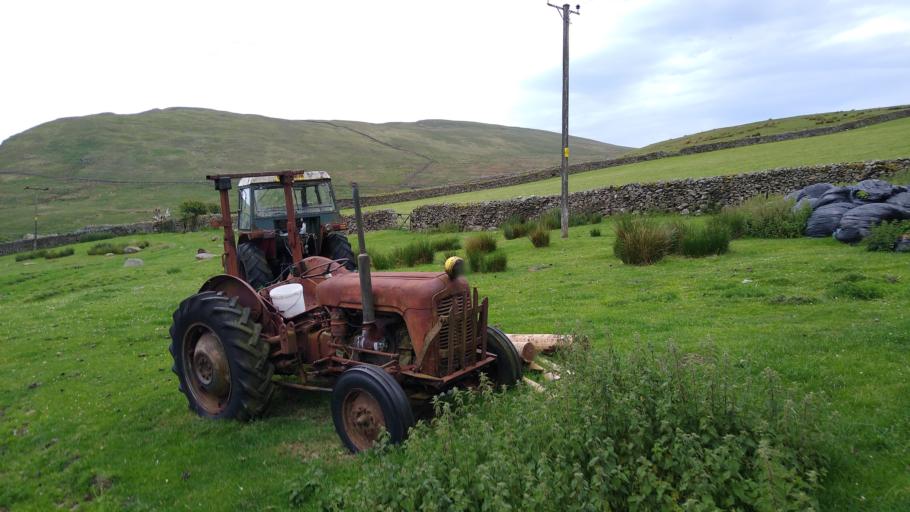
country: GB
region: England
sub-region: Cumbria
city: Millom
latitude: 54.2916
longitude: -3.2796
